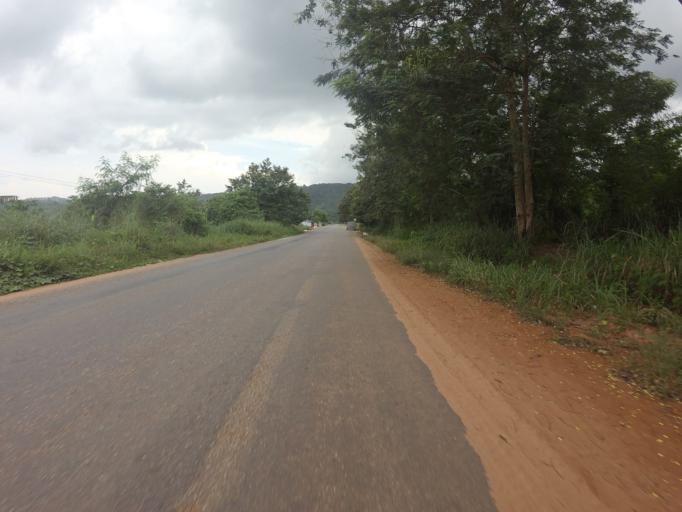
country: GH
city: Akropong
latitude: 5.9601
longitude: -0.1329
